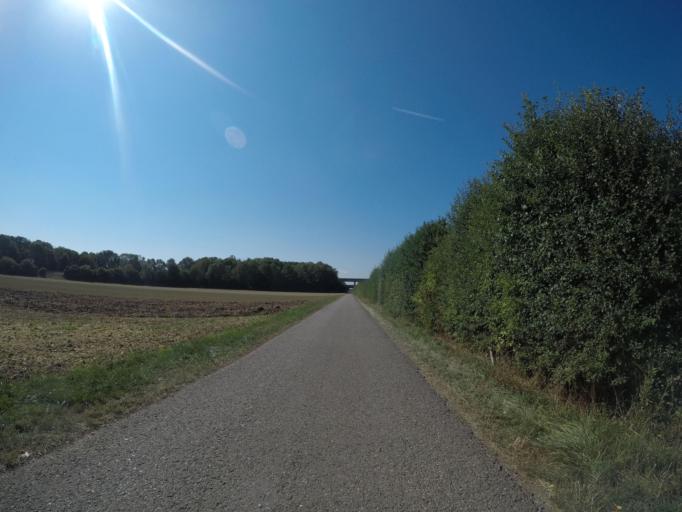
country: DE
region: Baden-Wuerttemberg
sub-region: Tuebingen Region
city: Langenau
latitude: 48.4685
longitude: 10.1118
